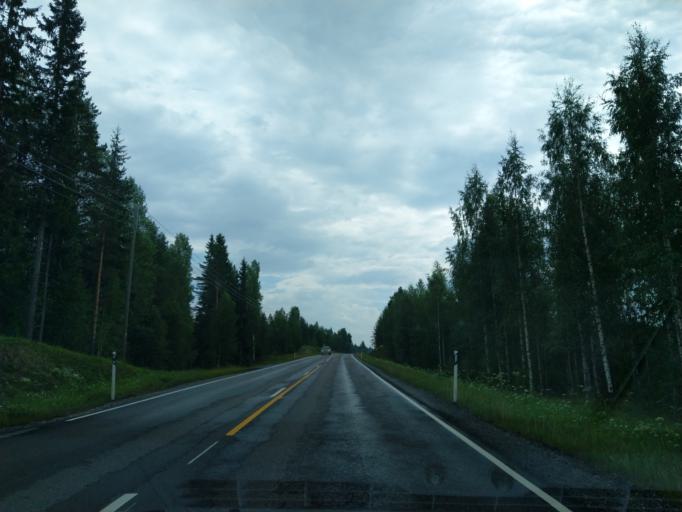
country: FI
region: South Karelia
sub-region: Imatra
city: Parikkala
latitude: 61.6426
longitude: 29.4259
